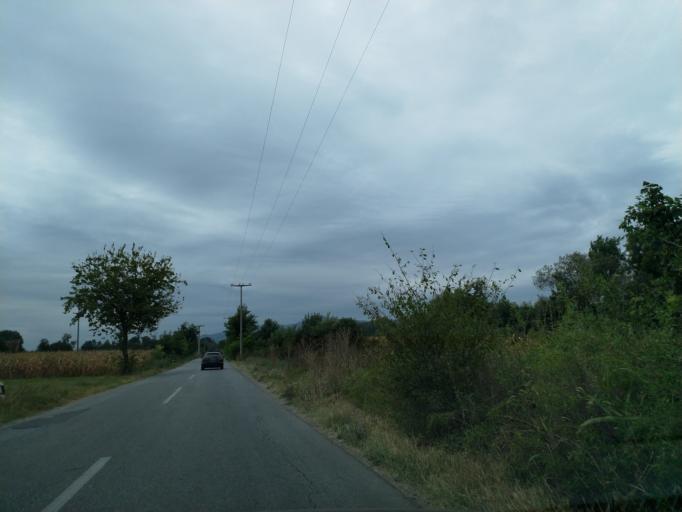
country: RS
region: Central Serbia
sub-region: Pomoravski Okrug
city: Paracin
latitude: 43.8476
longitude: 21.3820
